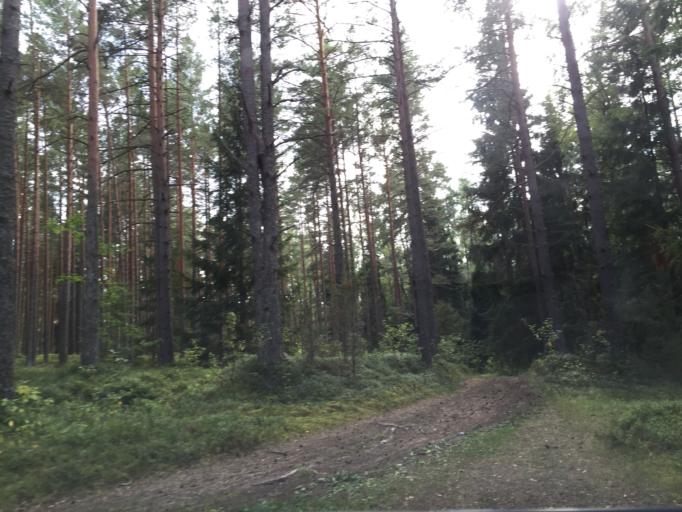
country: LV
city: Tireli
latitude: 56.8669
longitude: 23.6631
